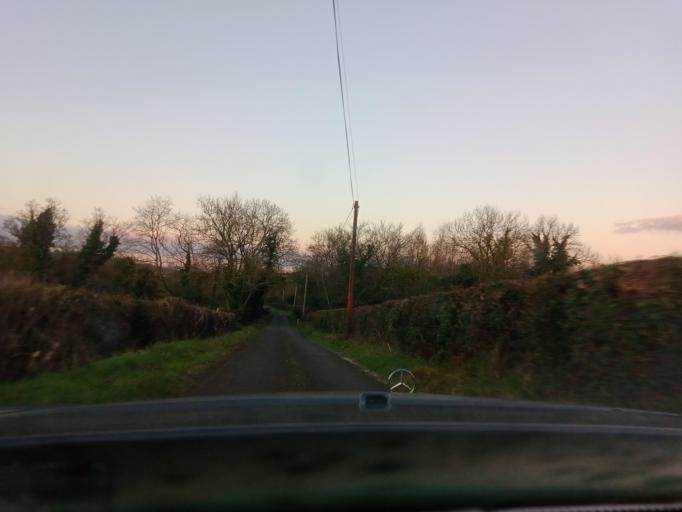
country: IE
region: Leinster
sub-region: Kilkenny
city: Graiguenamanagh
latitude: 52.5662
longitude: -6.9596
